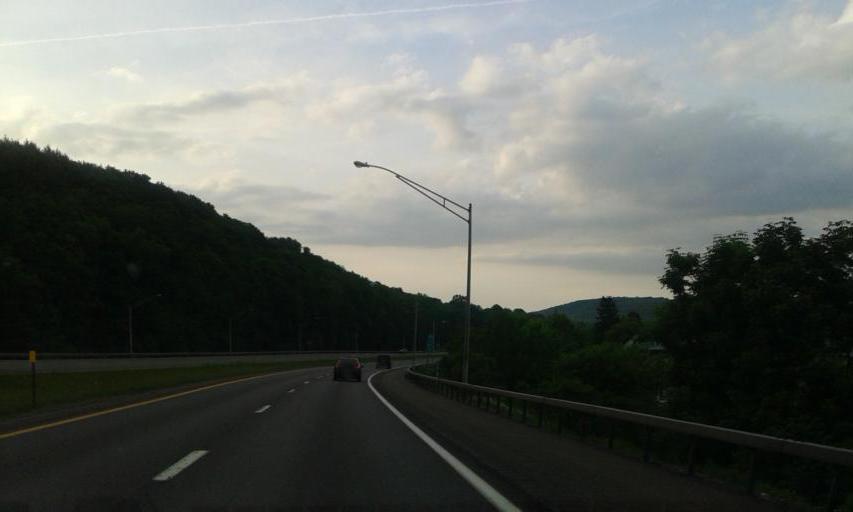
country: US
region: New York
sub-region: Broome County
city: Port Dickinson
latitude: 42.1538
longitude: -75.8975
